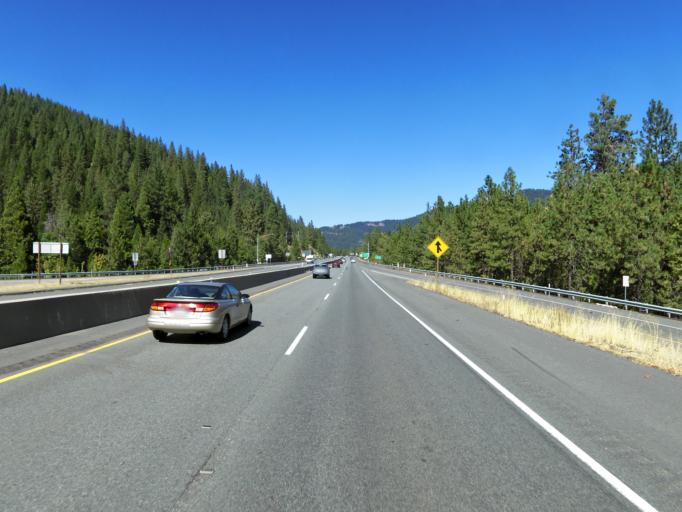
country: US
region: California
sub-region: Siskiyou County
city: Dunsmuir
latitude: 41.1829
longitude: -122.2903
